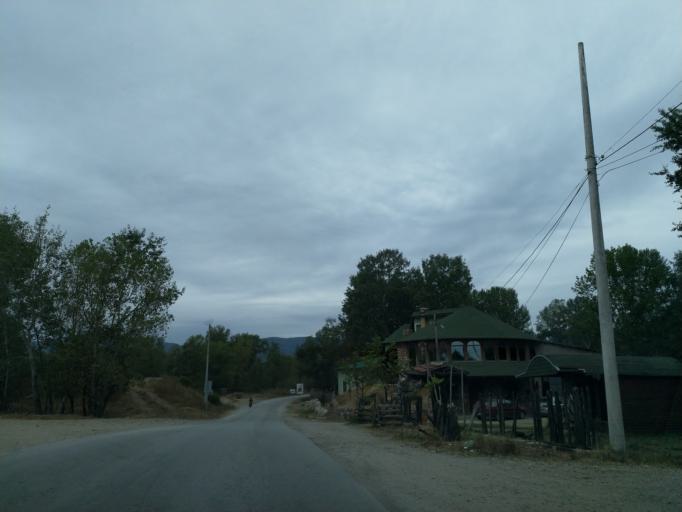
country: RS
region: Central Serbia
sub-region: Pomoravski Okrug
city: Paracin
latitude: 43.8264
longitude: 21.3528
